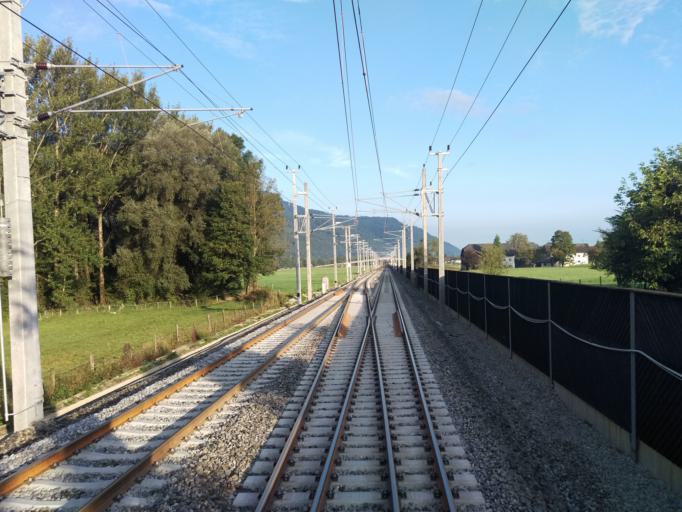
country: AT
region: Salzburg
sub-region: Politischer Bezirk Hallein
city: Golling an der Salzach
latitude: 47.6093
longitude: 13.1588
